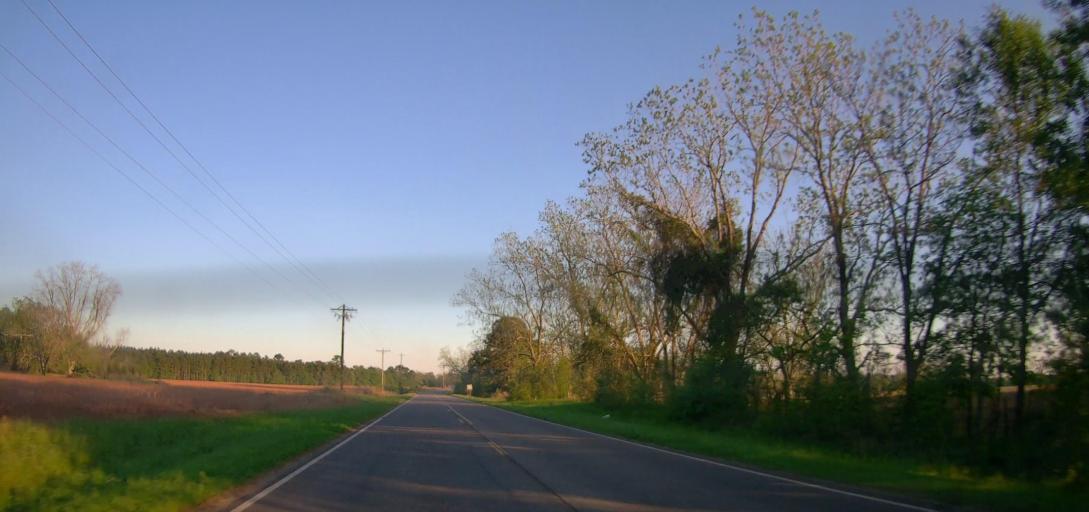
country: US
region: Georgia
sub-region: Irwin County
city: Ocilla
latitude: 31.6100
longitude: -83.2611
